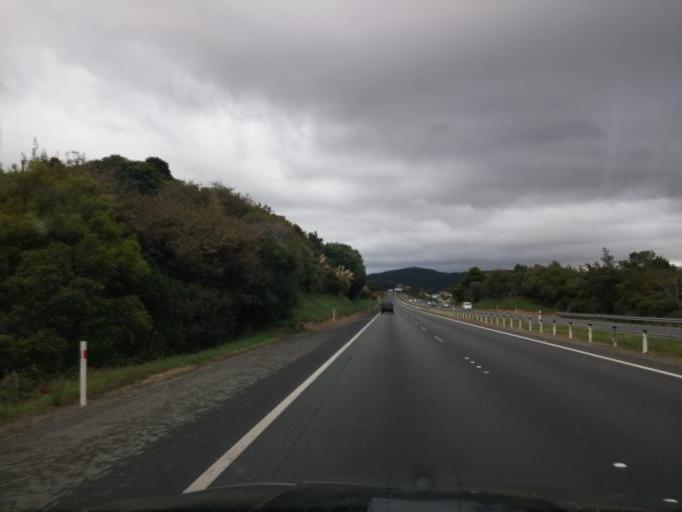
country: NZ
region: Wellington
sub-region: Porirua City
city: Porirua
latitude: -41.1617
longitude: 174.8357
